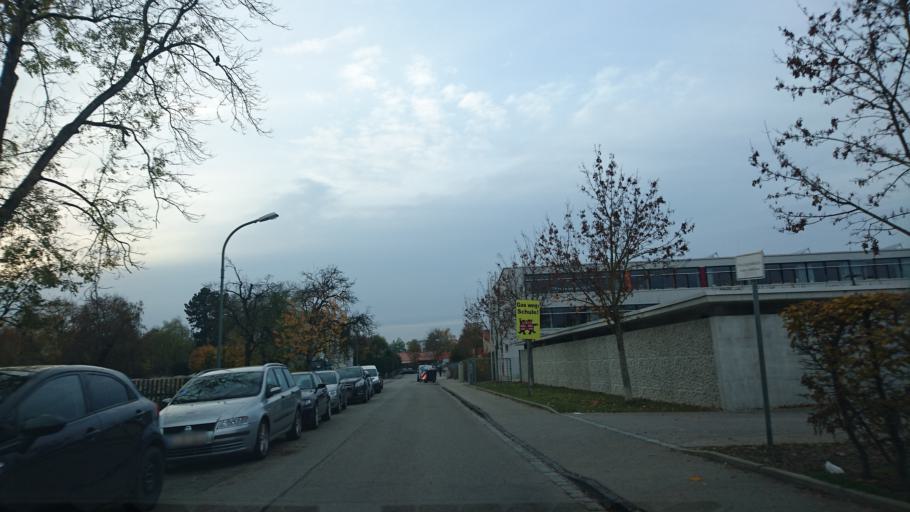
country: DE
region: Bavaria
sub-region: Swabia
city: Augsburg
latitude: 48.3916
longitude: 10.8855
